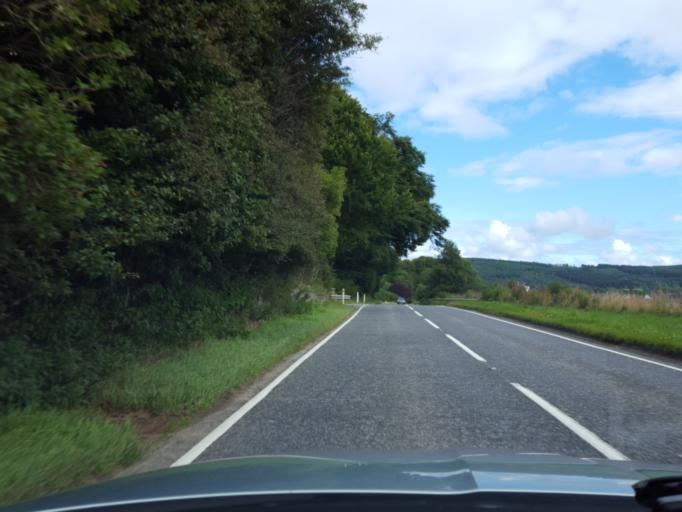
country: GB
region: Scotland
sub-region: Moray
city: Rothes
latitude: 57.5180
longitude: -3.2091
